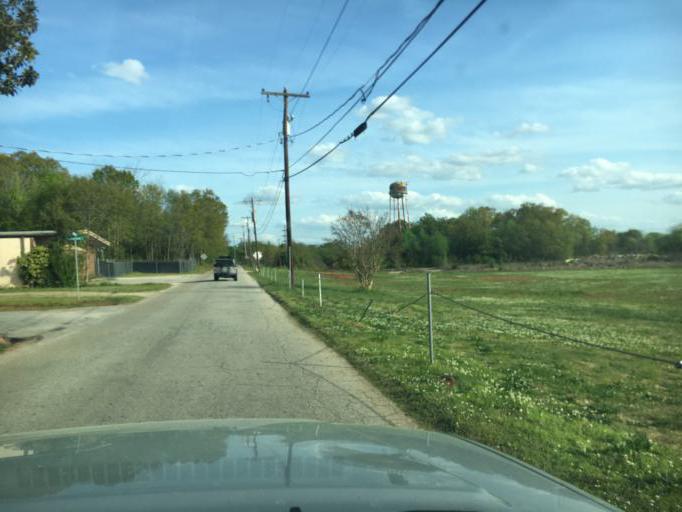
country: US
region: South Carolina
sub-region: Greenville County
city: Sans Souci
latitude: 34.8684
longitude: -82.4201
